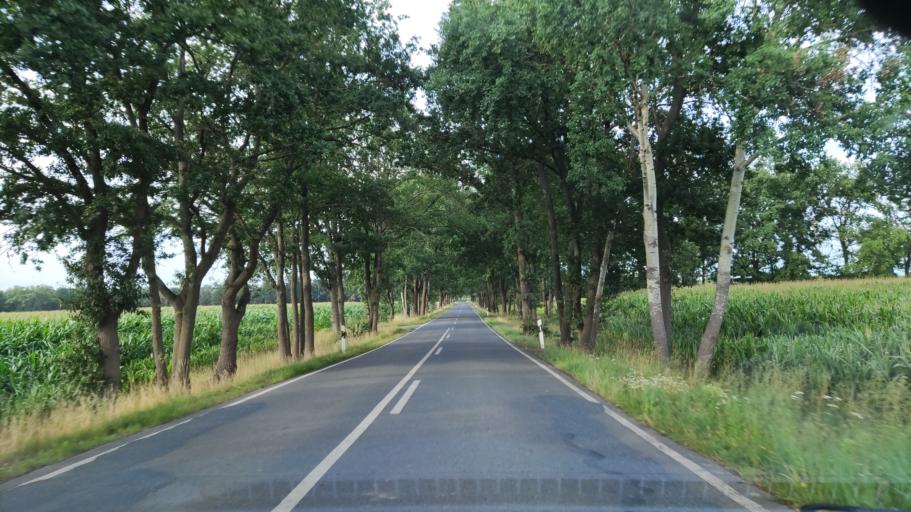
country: DE
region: Lower Saxony
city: Jameln
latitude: 53.0499
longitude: 11.1335
